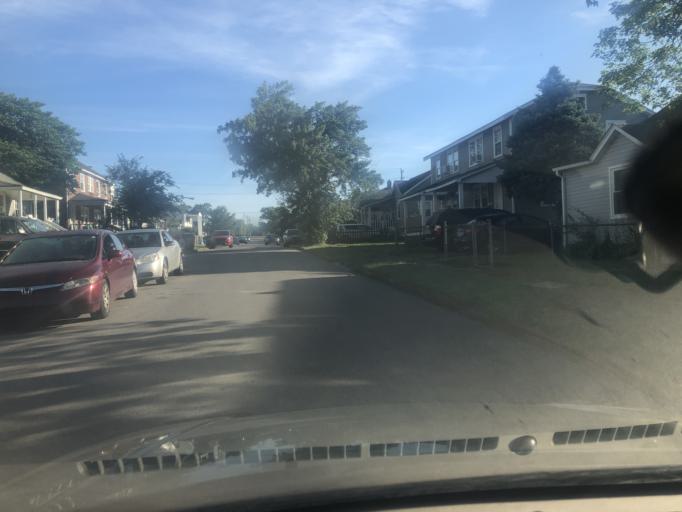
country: US
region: Tennessee
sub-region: Davidson County
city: Lakewood
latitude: 36.2599
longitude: -86.6497
